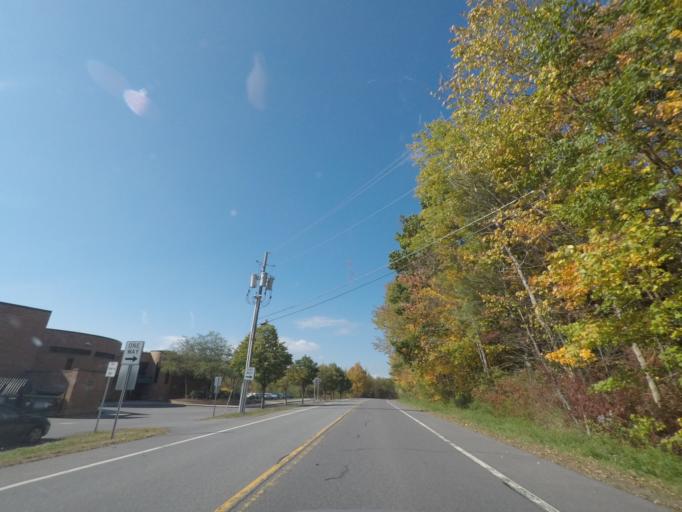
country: US
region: New York
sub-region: Rensselaer County
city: Averill Park
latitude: 42.6385
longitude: -73.5426
